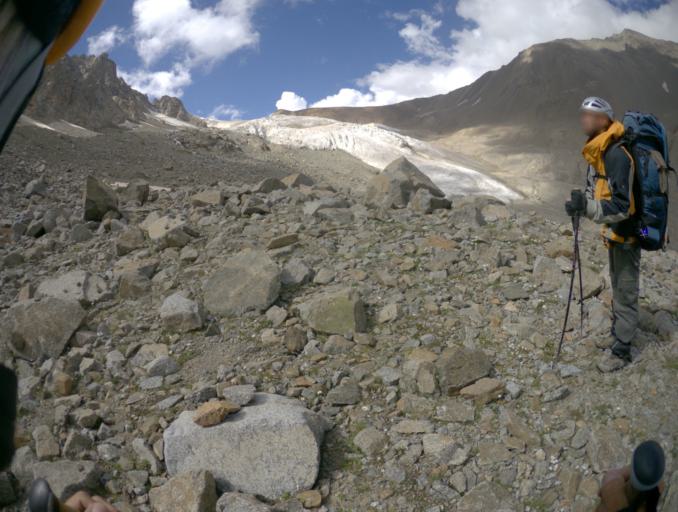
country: RU
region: Kabardino-Balkariya
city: Terskol
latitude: 43.3333
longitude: 42.5470
